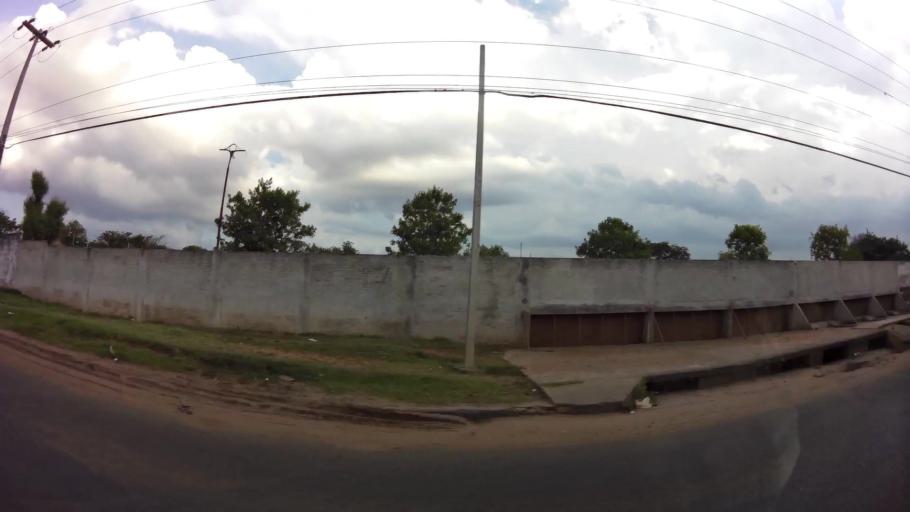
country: PY
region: Central
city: Villa Elisa
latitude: -25.3567
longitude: -57.5608
